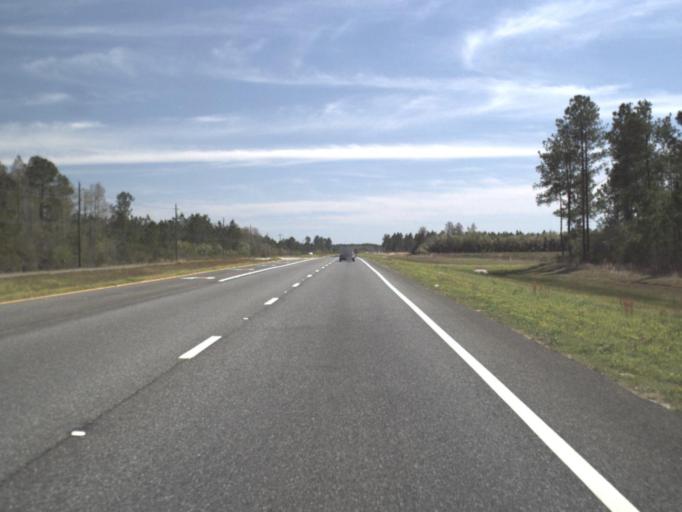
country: US
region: Florida
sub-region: Bay County
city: Lynn Haven
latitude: 30.3605
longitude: -85.6699
